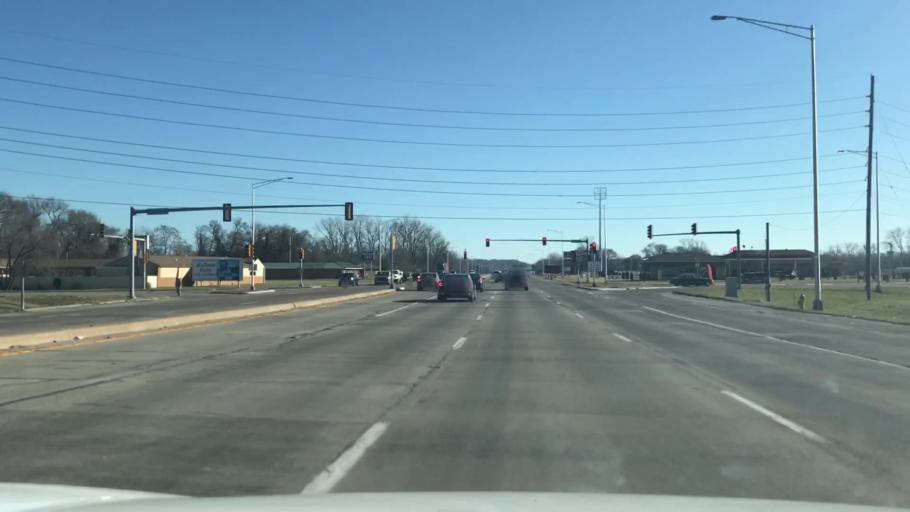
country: US
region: Illinois
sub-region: Saint Clair County
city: Alorton
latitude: 38.5921
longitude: -90.1190
